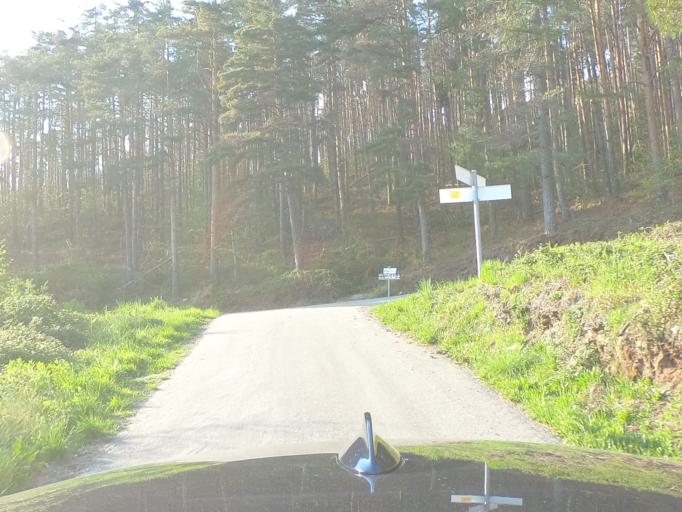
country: PT
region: Vila Real
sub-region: Vila Real
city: Vila Real
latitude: 41.3179
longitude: -7.8637
